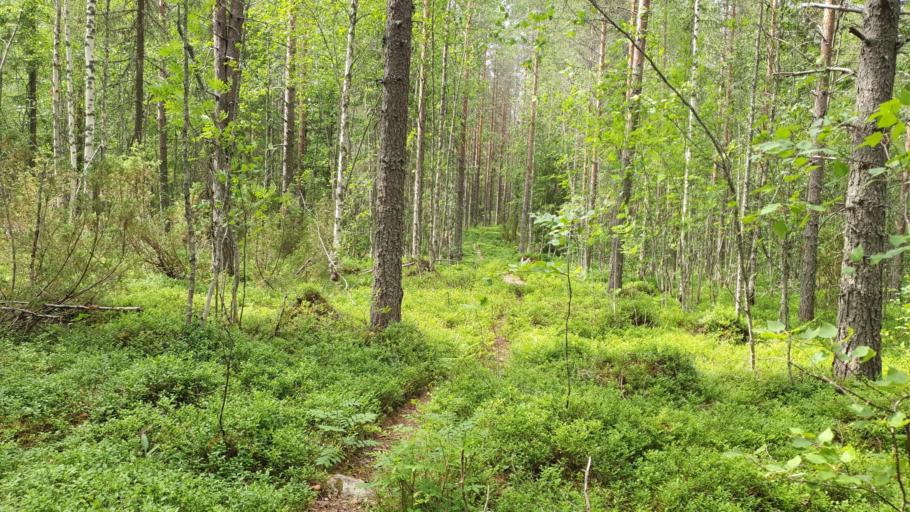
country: FI
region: Kainuu
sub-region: Kehys-Kainuu
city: Kuhmo
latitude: 63.9890
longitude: 29.4344
